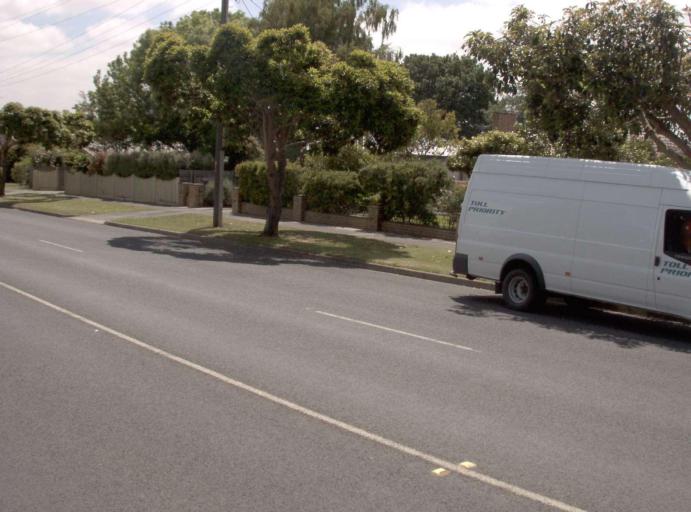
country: AU
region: Victoria
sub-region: Baw Baw
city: Warragul
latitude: -38.4735
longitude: 145.9484
